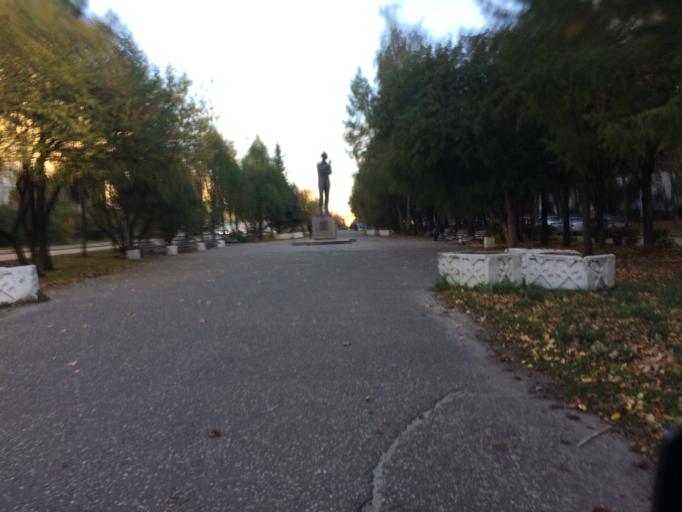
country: RU
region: Mariy-El
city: Yoshkar-Ola
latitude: 56.6315
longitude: 47.9135
